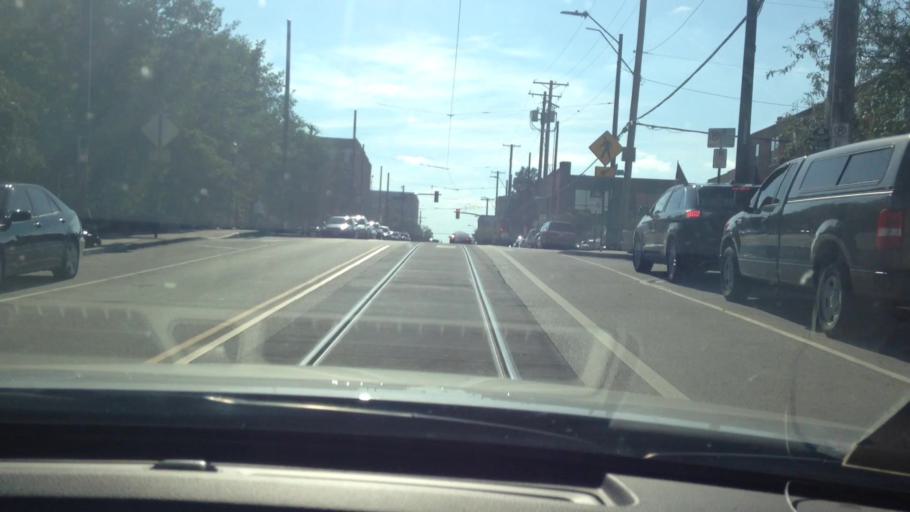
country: US
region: Missouri
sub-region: Jackson County
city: Kansas City
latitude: 39.1100
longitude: -94.5829
